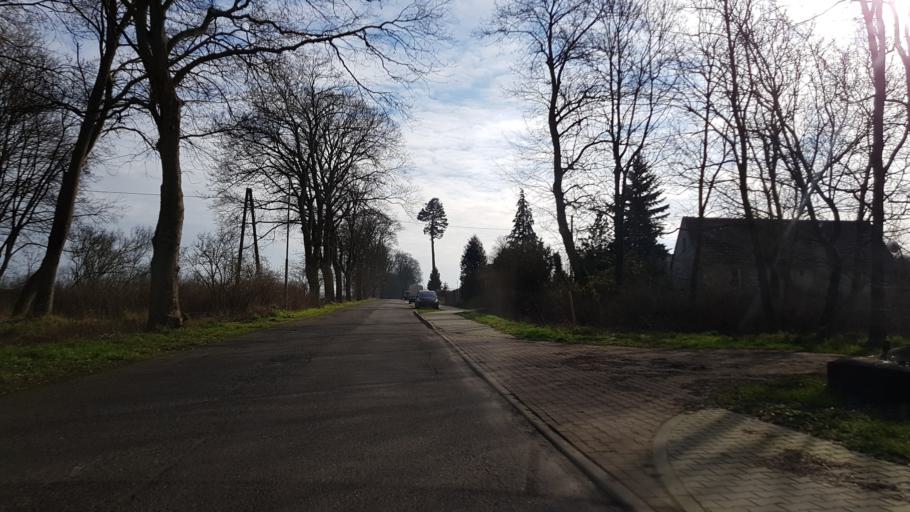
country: PL
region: West Pomeranian Voivodeship
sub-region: Powiat policki
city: Dobra
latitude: 53.5531
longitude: 14.3096
